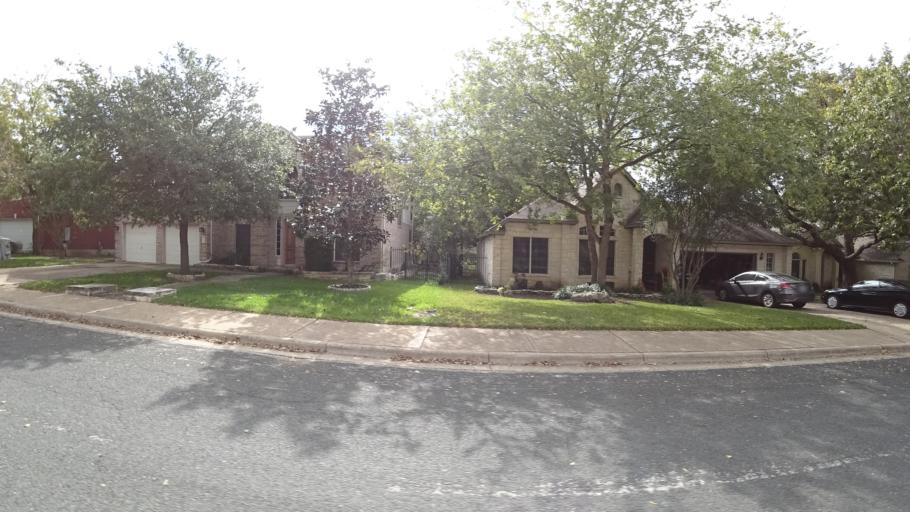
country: US
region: Texas
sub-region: Travis County
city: Shady Hollow
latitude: 30.1566
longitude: -97.8535
